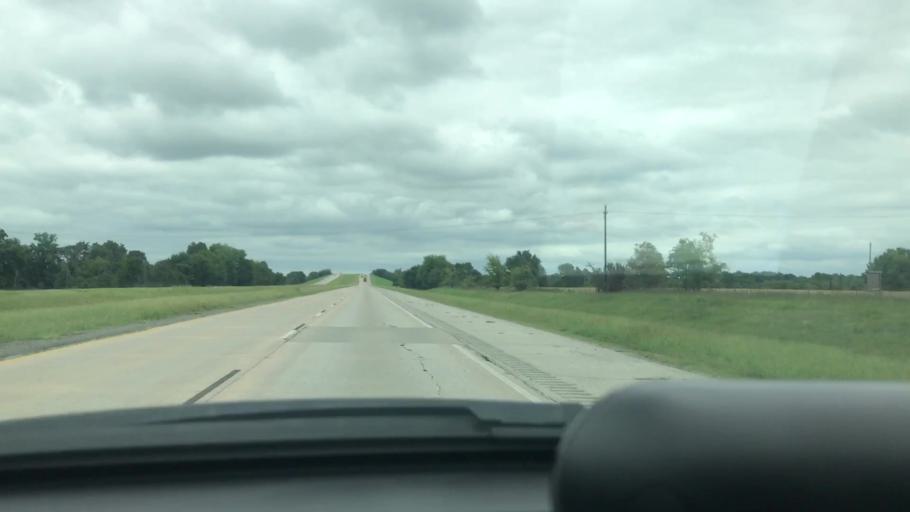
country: US
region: Oklahoma
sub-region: Wagoner County
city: Wagoner
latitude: 35.8742
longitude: -95.4017
